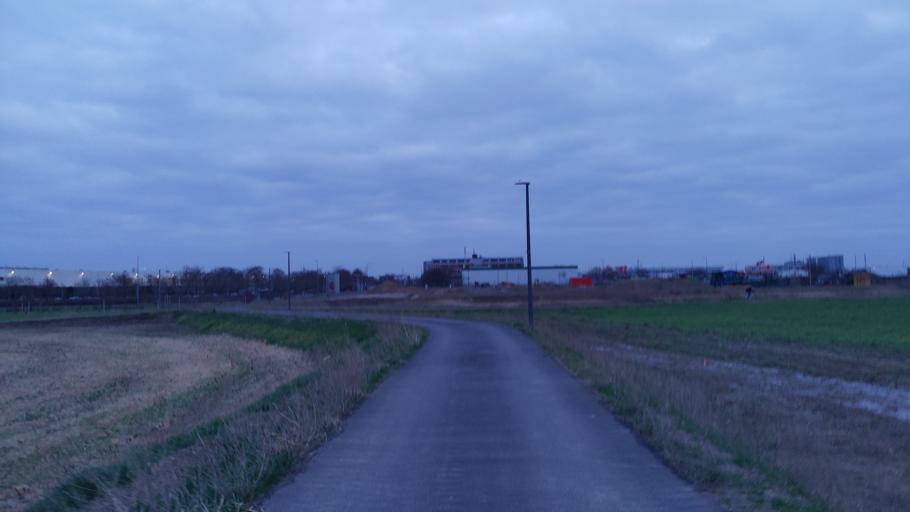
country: DE
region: North Rhine-Westphalia
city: Monheim am Rhein
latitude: 51.0412
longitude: 6.9112
